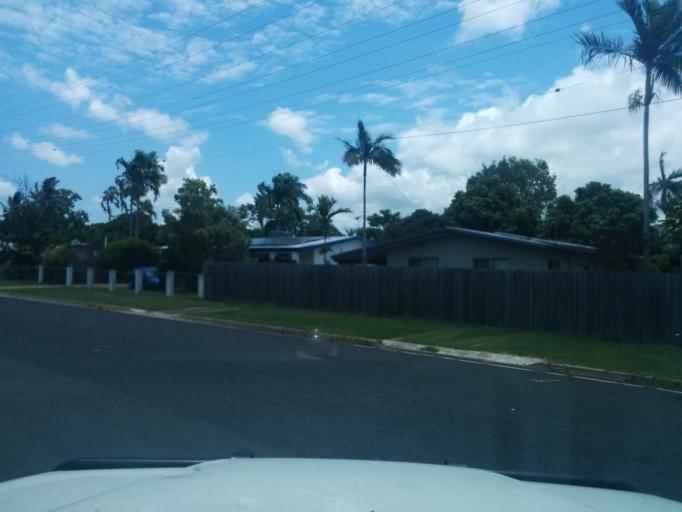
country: AU
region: Queensland
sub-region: Cairns
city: Trinity Beach
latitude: -16.8038
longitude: 145.7003
